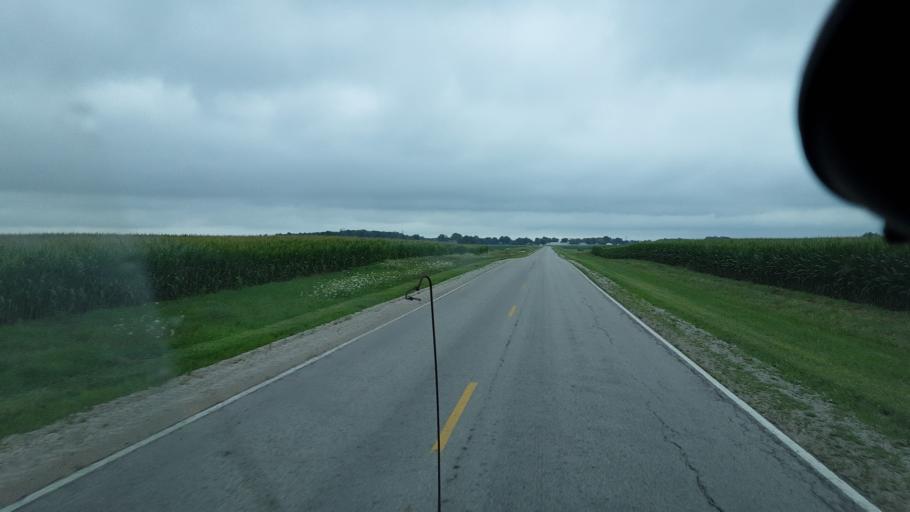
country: US
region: Indiana
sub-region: Wells County
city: Bluffton
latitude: 40.7957
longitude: -85.0909
